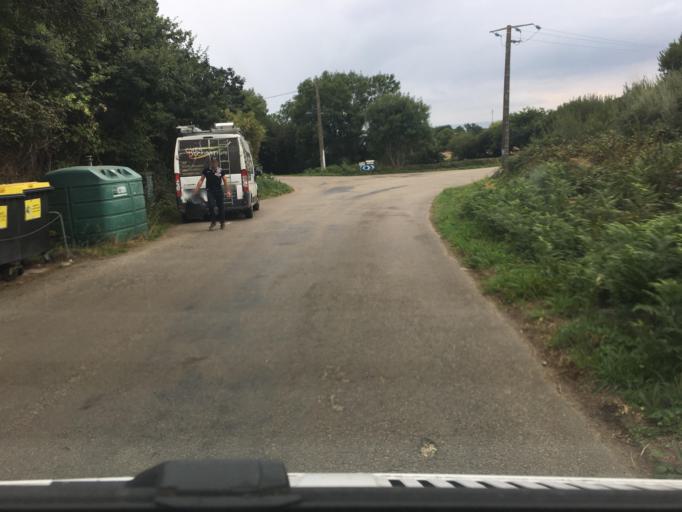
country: FR
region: Brittany
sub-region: Departement du Finistere
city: Beuzec-Cap-Sizun
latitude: 48.0794
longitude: -4.4776
